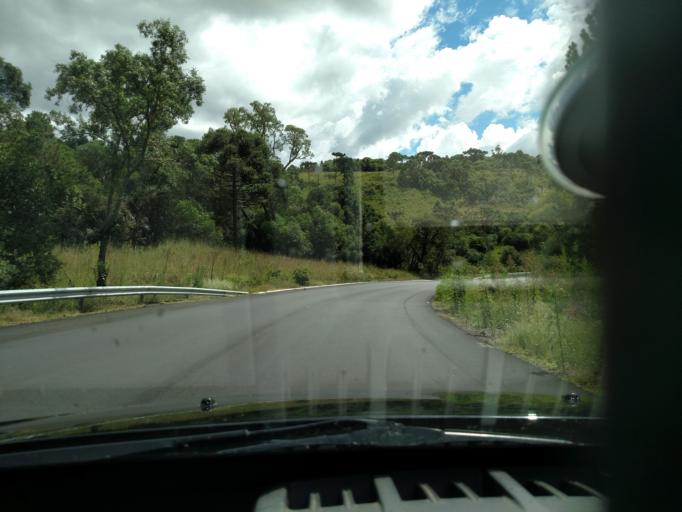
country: BR
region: Santa Catarina
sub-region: Sao Joaquim
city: Sao Joaquim
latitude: -28.1299
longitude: -50.0472
